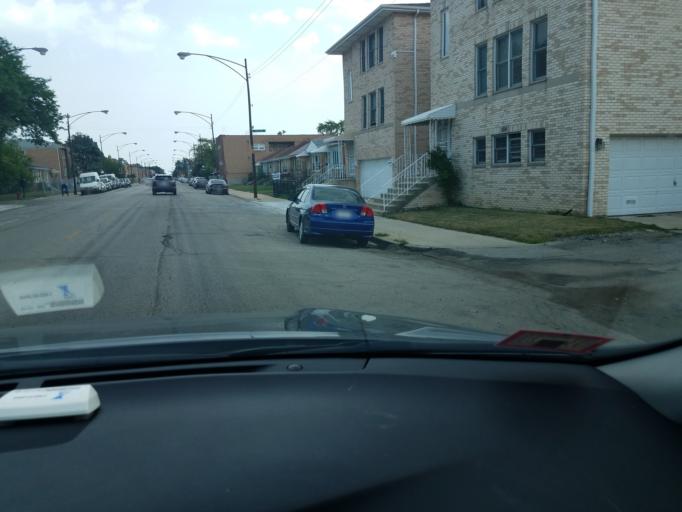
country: US
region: Illinois
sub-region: Cook County
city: Niles
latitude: 41.9918
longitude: -87.7816
